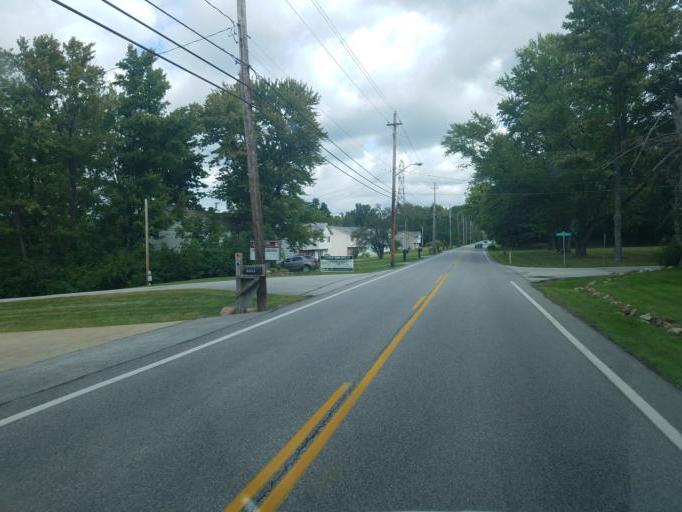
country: US
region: Ohio
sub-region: Lake County
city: Painesville
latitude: 41.7202
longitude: -81.1975
